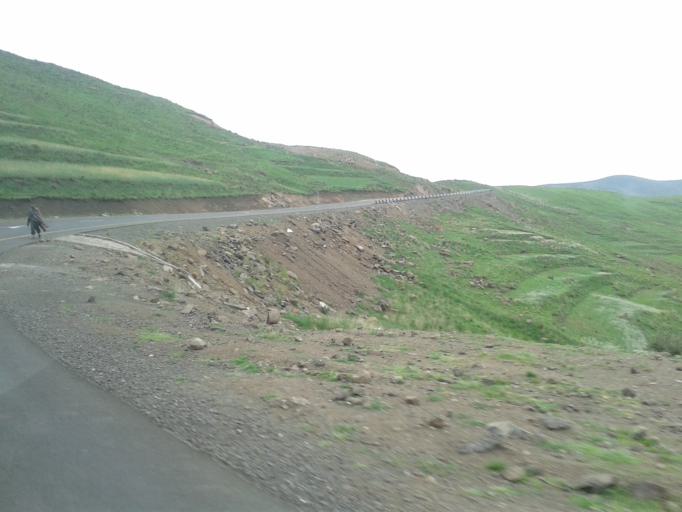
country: LS
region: Maseru
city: Nako
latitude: -29.7867
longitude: 28.0217
